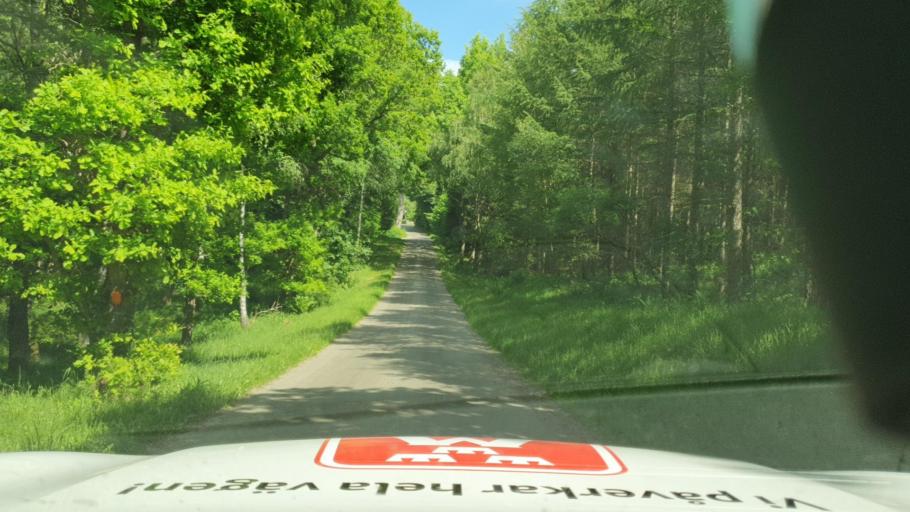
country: SE
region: Skane
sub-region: Lunds Kommun
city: Genarp
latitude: 55.5597
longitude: 13.3982
